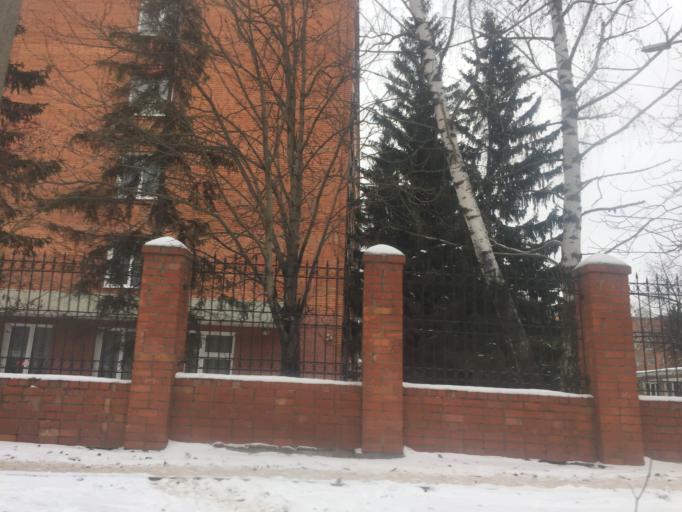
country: RU
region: Tula
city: Tula
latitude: 54.1737
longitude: 37.6334
